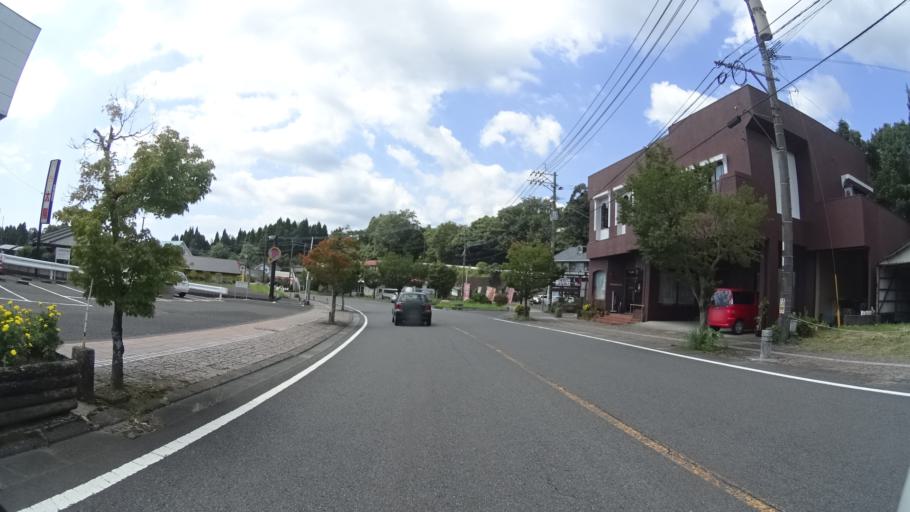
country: JP
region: Kagoshima
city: Kokubu-matsuki
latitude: 31.8862
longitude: 130.8181
